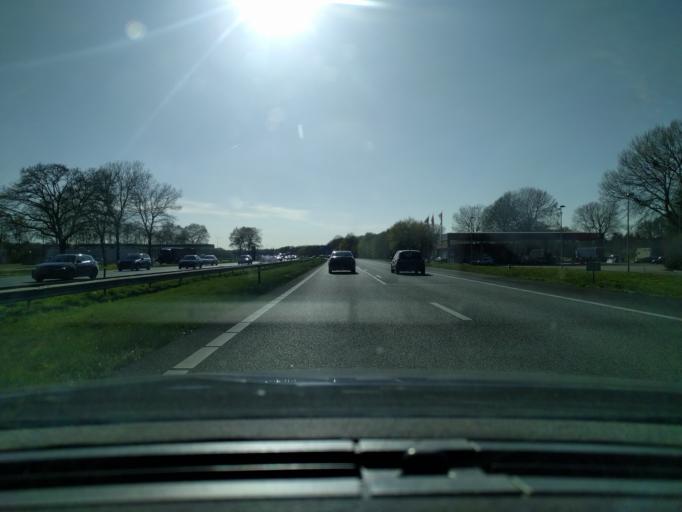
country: NL
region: North Brabant
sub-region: Gemeente Landerd
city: Schaijk
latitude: 51.7464
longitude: 5.6028
